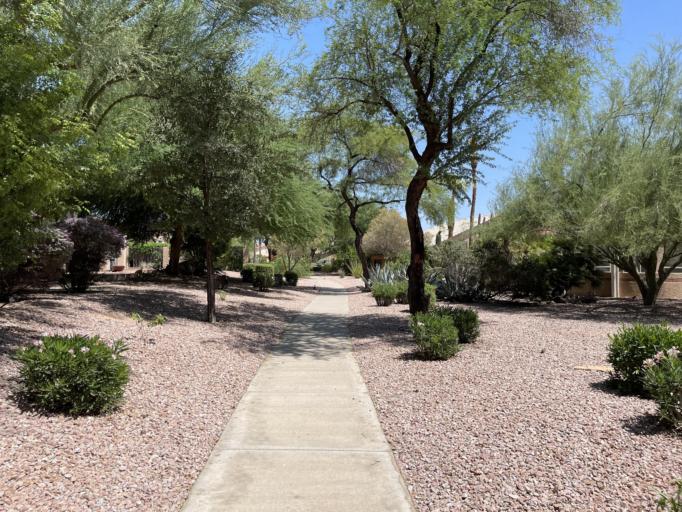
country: US
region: Arizona
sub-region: Maricopa County
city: Sun Lakes
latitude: 33.2279
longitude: -111.8776
